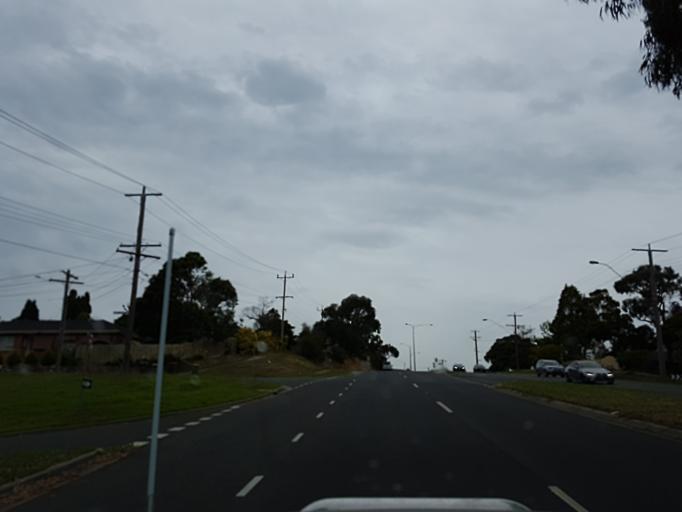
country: AU
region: Victoria
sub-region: Knox
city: Bayswater
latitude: -37.8587
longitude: 145.2620
